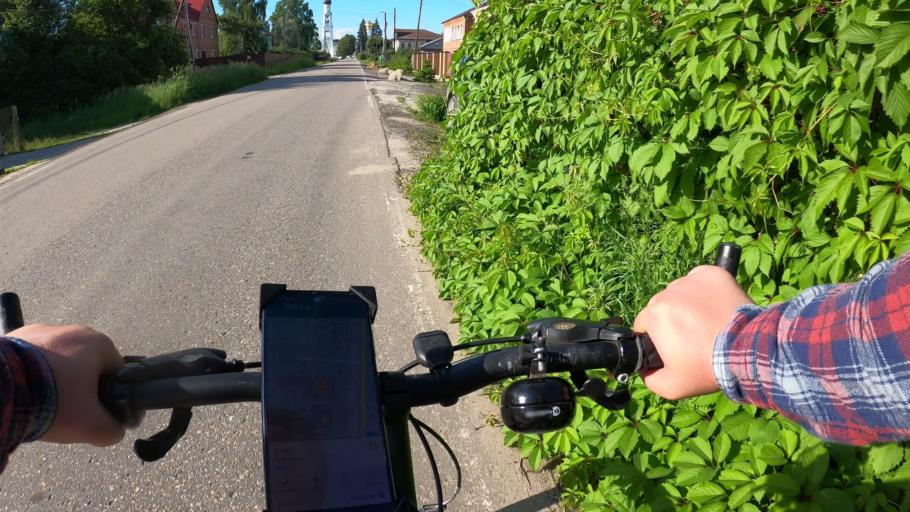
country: RU
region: Moskovskaya
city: Ashitkovo
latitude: 55.4364
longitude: 38.6046
